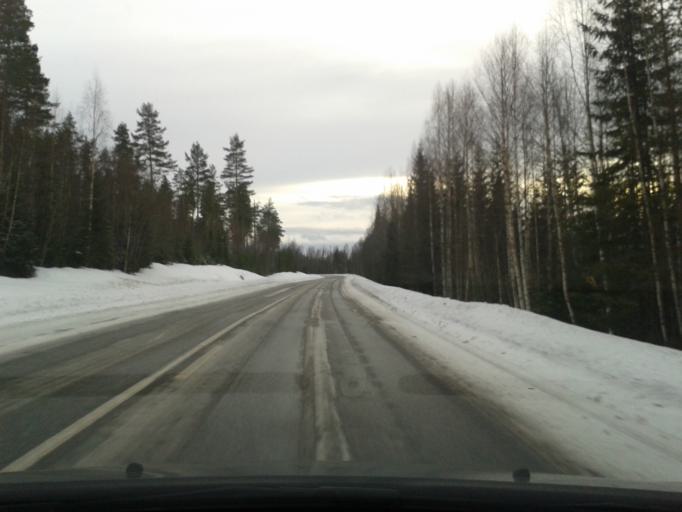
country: SE
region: Vaesternorrland
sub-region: Solleftea Kommun
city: As
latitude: 63.6665
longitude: 16.7889
